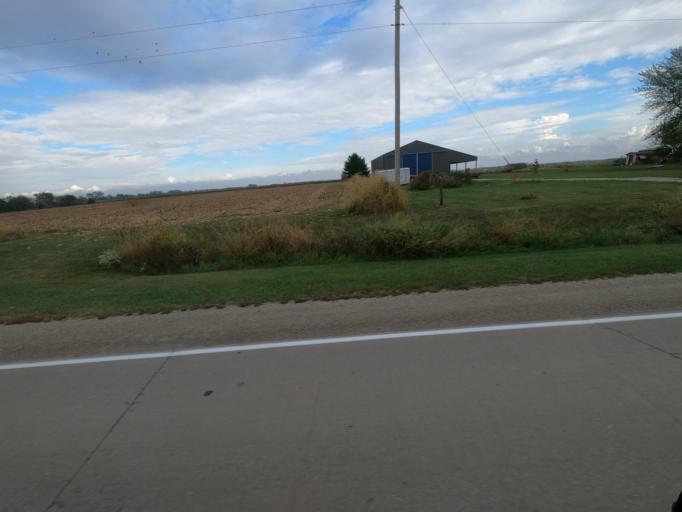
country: US
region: Iowa
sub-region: Henry County
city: Mount Pleasant
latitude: 40.8023
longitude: -91.7042
